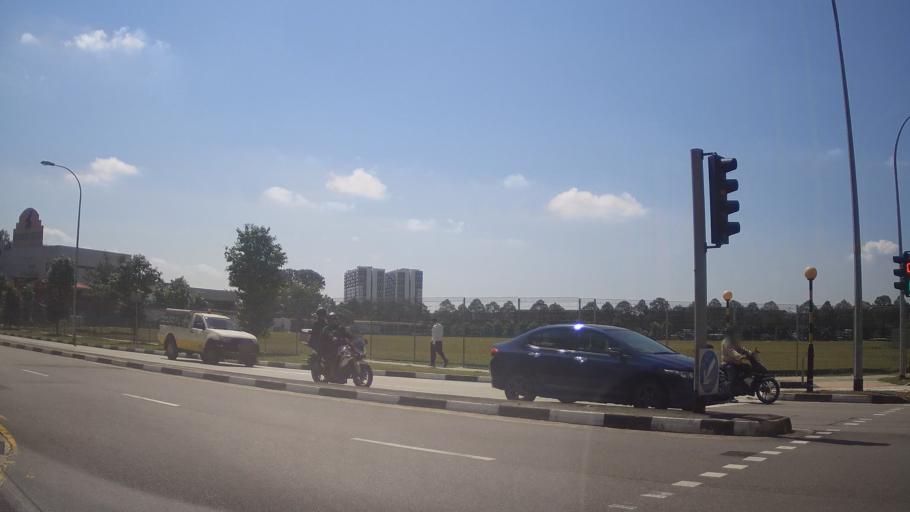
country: SG
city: Singapore
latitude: 1.3266
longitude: 103.7228
